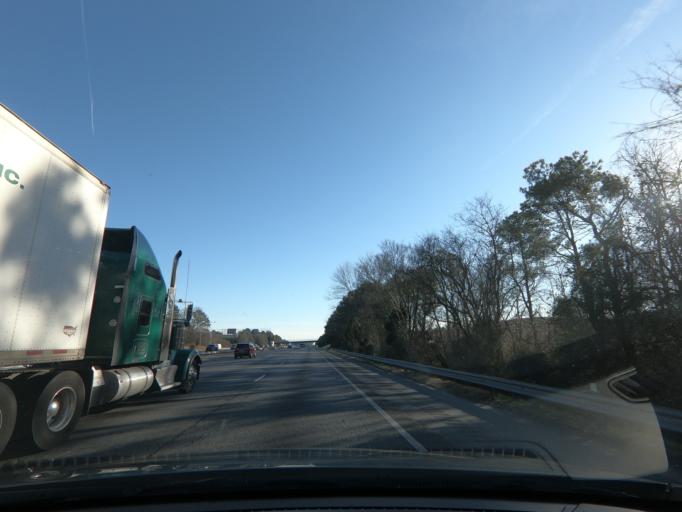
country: US
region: Georgia
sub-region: Bartow County
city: Adairsville
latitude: 34.4060
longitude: -84.9193
